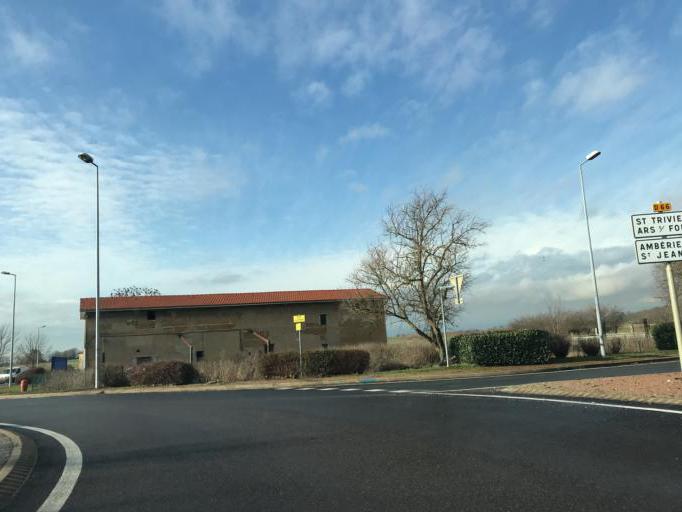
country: FR
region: Rhone-Alpes
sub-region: Departement de l'Ain
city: Civrieux
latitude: 45.9350
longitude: 4.8823
